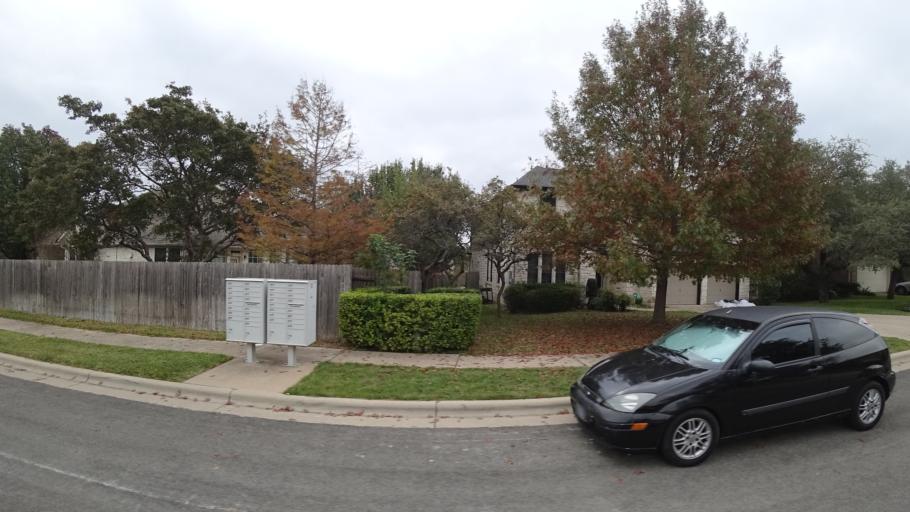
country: US
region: Texas
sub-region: Williamson County
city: Anderson Mill
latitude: 30.4330
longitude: -97.8320
